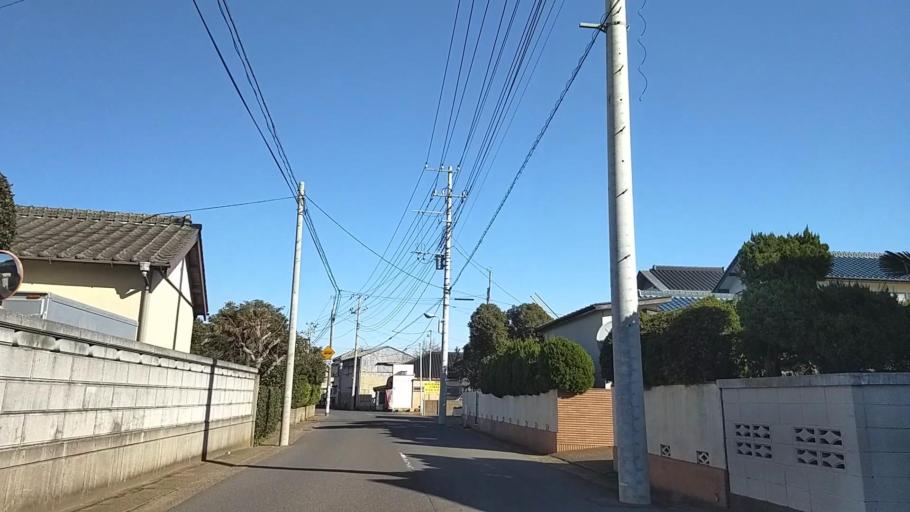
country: JP
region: Chiba
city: Hasaki
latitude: 35.7280
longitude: 140.8364
